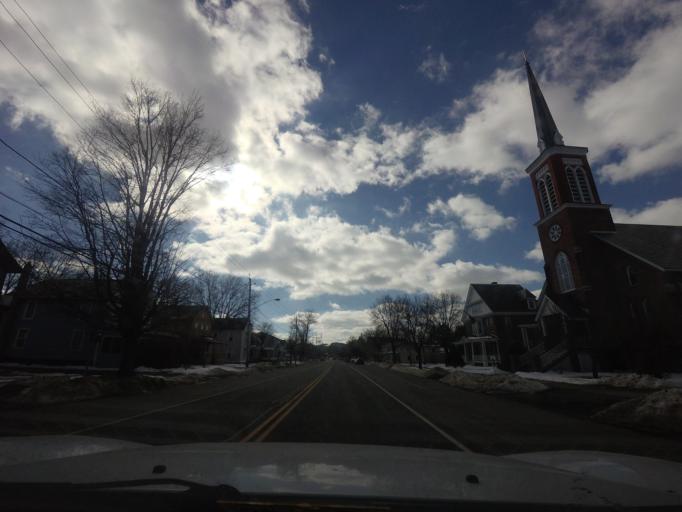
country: US
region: New York
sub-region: Washington County
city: Cambridge
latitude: 43.1763
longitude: -73.3279
